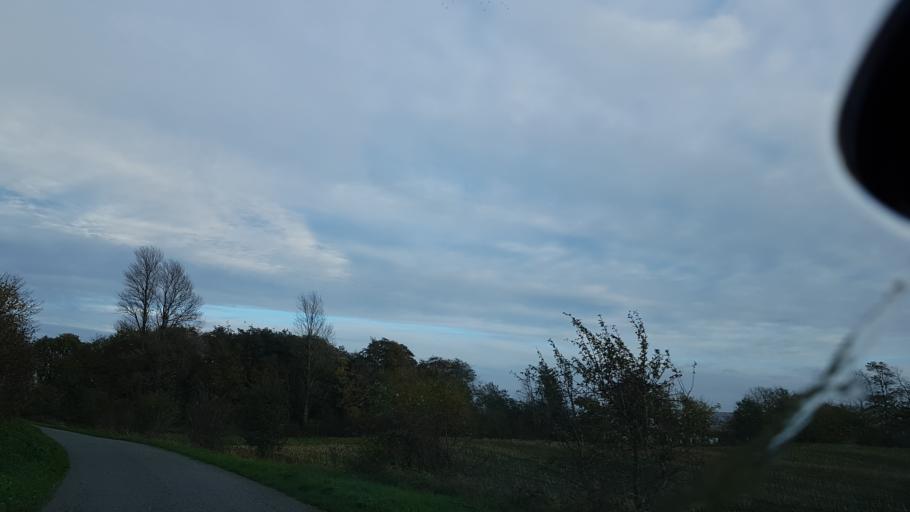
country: DK
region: South Denmark
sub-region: Haderslev Kommune
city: Vojens
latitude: 55.3212
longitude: 9.3672
